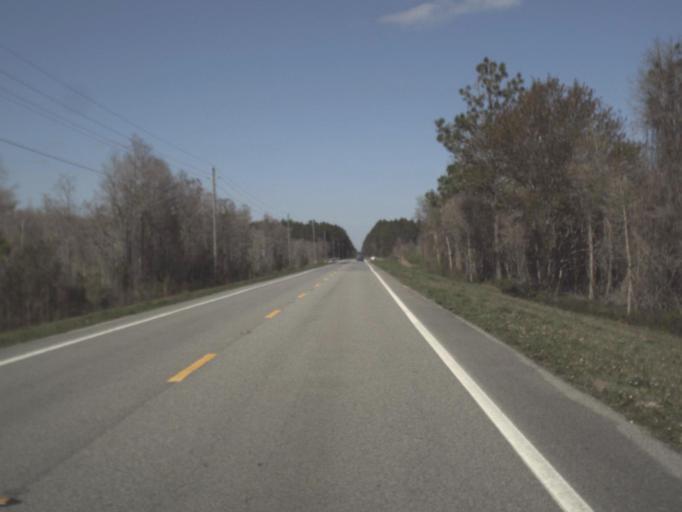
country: US
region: Florida
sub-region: Gulf County
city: Wewahitchka
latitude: 29.9432
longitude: -85.1859
